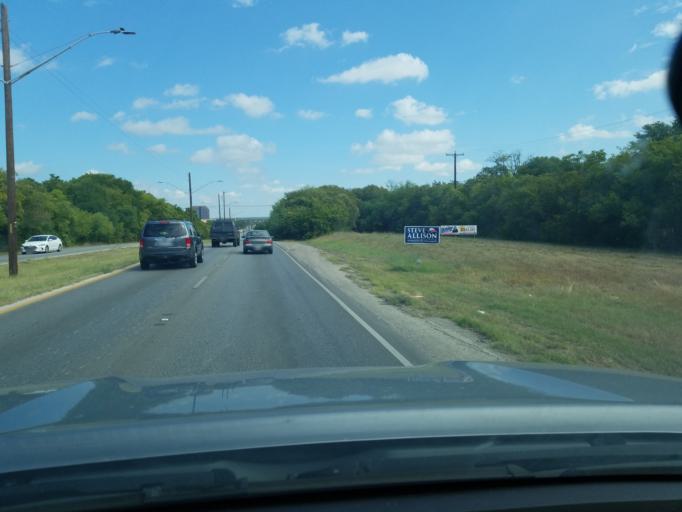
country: US
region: Texas
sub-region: Bexar County
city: Terrell Hills
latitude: 29.4986
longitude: -98.4345
